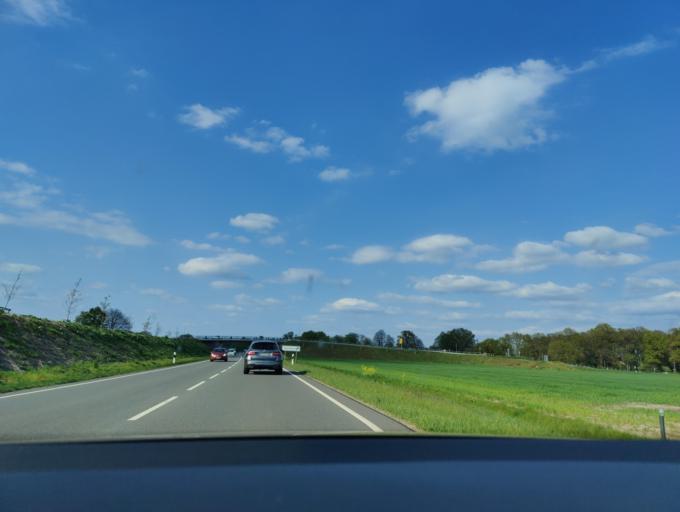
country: DE
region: Lower Saxony
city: Nordhorn
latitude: 52.4478
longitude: 7.0879
